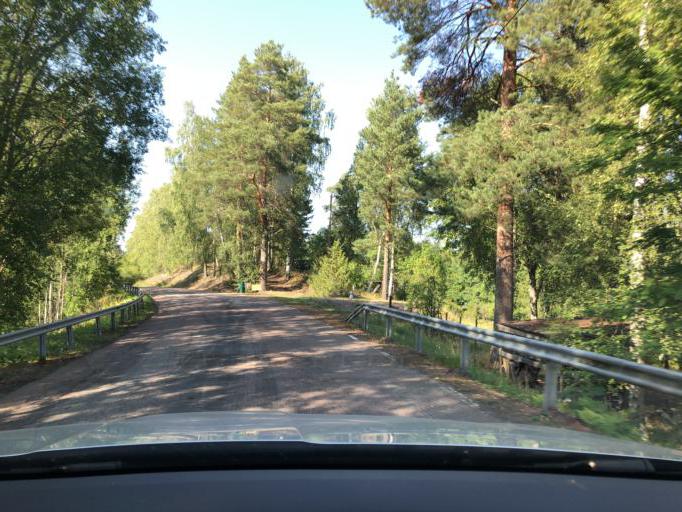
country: SE
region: Dalarna
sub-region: Hedemora Kommun
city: Hedemora
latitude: 60.3463
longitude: 15.9290
